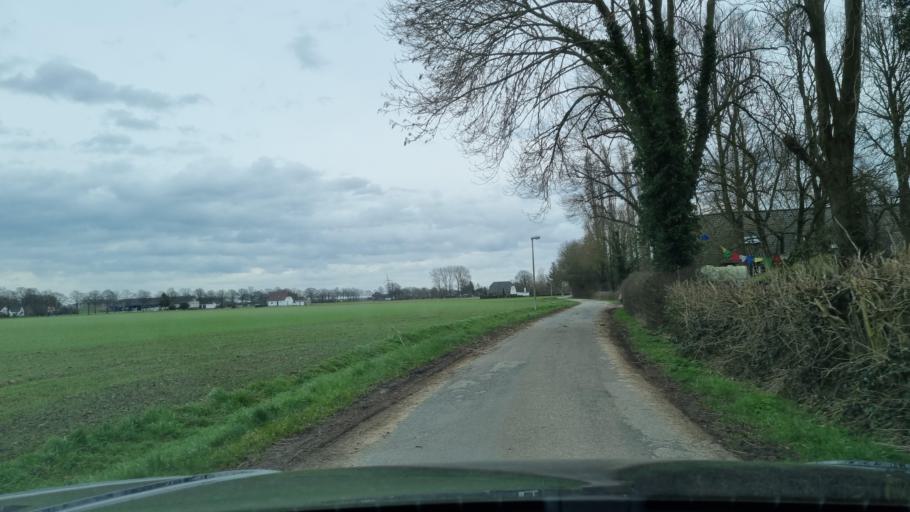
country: DE
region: North Rhine-Westphalia
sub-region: Regierungsbezirk Dusseldorf
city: Kleve
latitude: 51.8422
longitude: 6.0804
